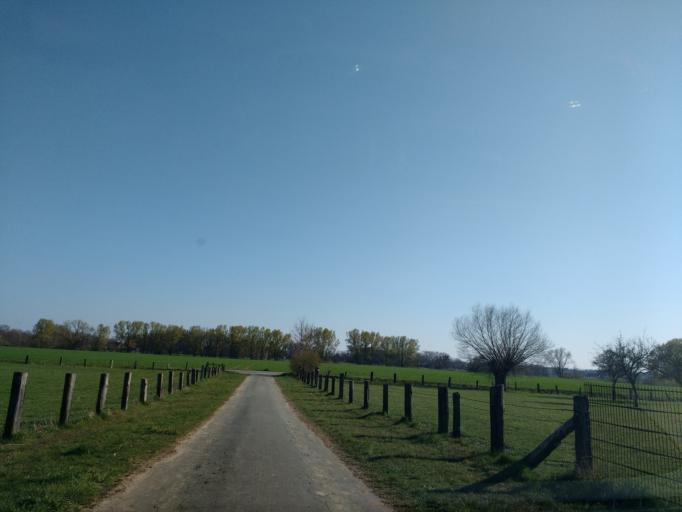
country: DE
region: North Rhine-Westphalia
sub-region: Regierungsbezirk Detmold
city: Delbruck
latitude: 51.7234
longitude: 8.5516
